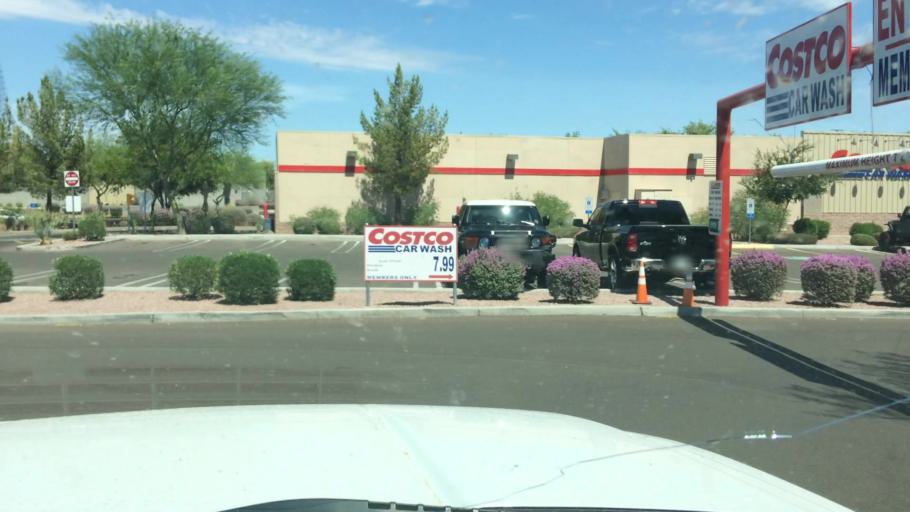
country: US
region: Arizona
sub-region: Maricopa County
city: Sun City
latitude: 33.6419
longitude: -112.2320
